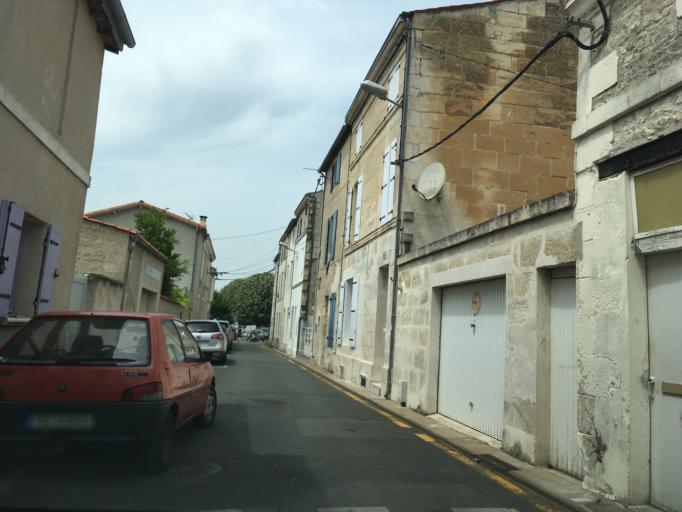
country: FR
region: Poitou-Charentes
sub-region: Departement des Deux-Sevres
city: Niort
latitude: 46.3189
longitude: -0.4611
